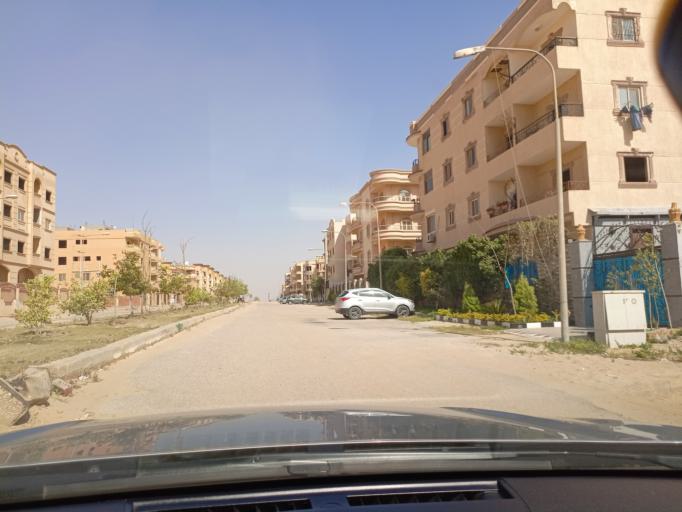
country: EG
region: Muhafazat al Qalyubiyah
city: Al Khankah
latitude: 30.2218
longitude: 31.4403
